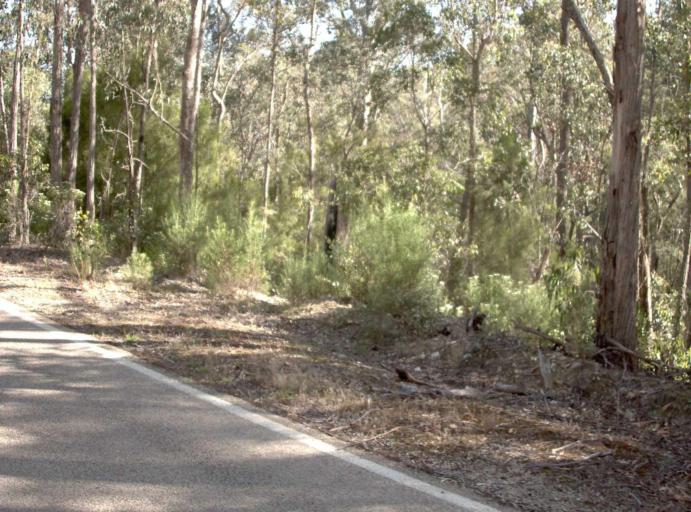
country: AU
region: Victoria
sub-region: East Gippsland
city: Lakes Entrance
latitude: -37.5430
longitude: 148.5468
